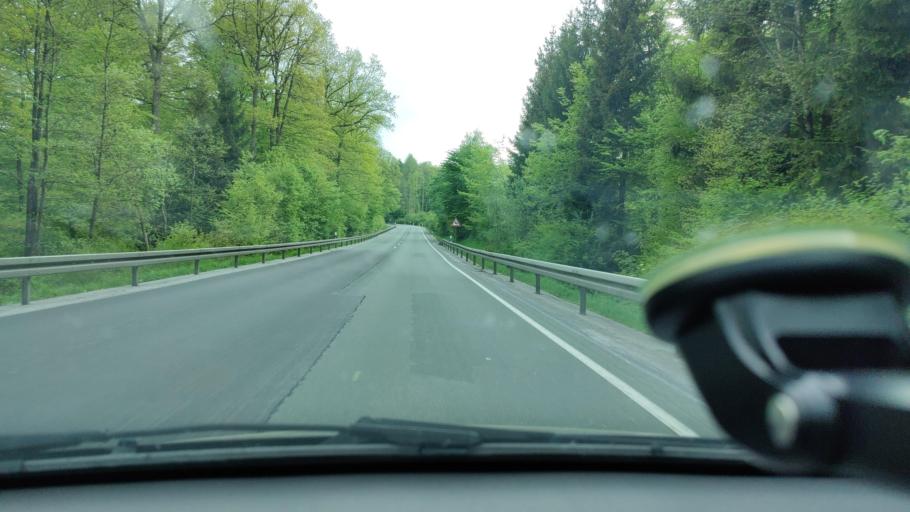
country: DE
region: North Rhine-Westphalia
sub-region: Regierungsbezirk Detmold
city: Wunnenberg
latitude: 51.4894
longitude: 8.6606
